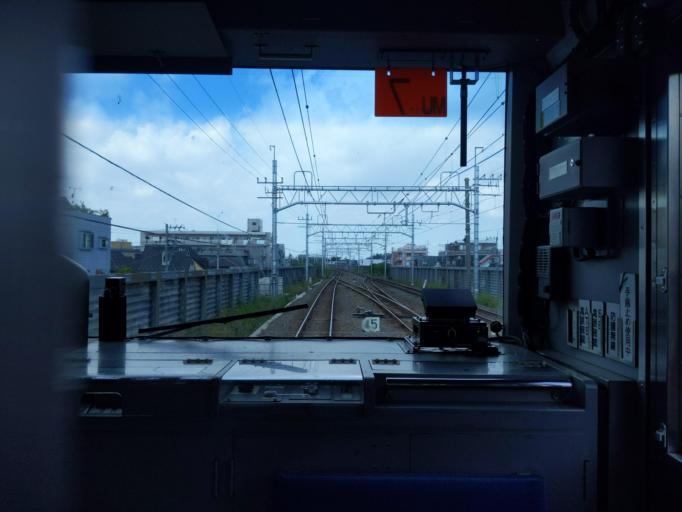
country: JP
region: Chiba
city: Nagareyama
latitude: 35.8398
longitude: 139.9024
